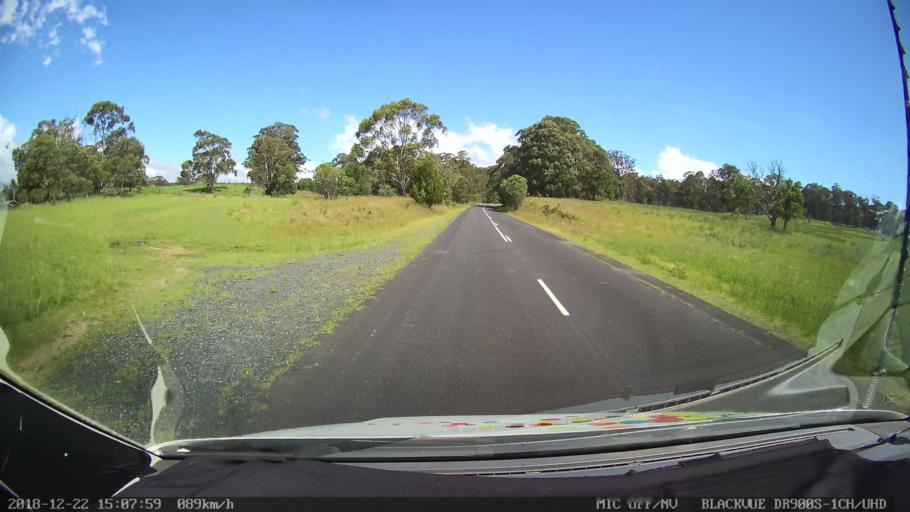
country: AU
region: New South Wales
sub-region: Bellingen
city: Dorrigo
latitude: -30.3063
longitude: 152.4131
